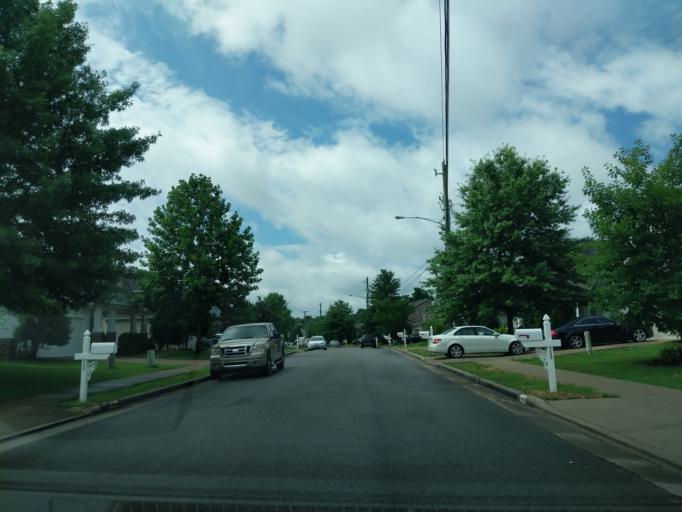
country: US
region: Tennessee
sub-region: Davidson County
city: Lakewood
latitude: 36.2383
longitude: -86.6942
